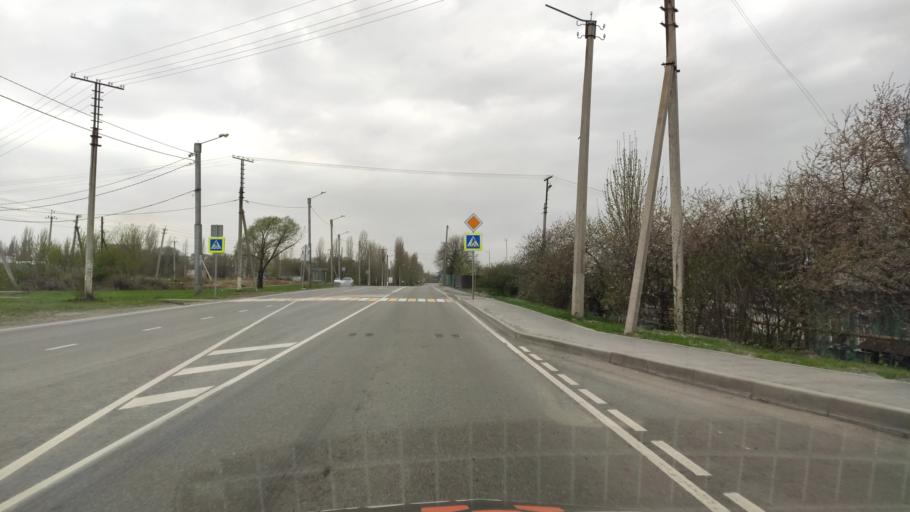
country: RU
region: Belgorod
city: Staryy Oskol
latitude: 51.2836
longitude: 37.7798
